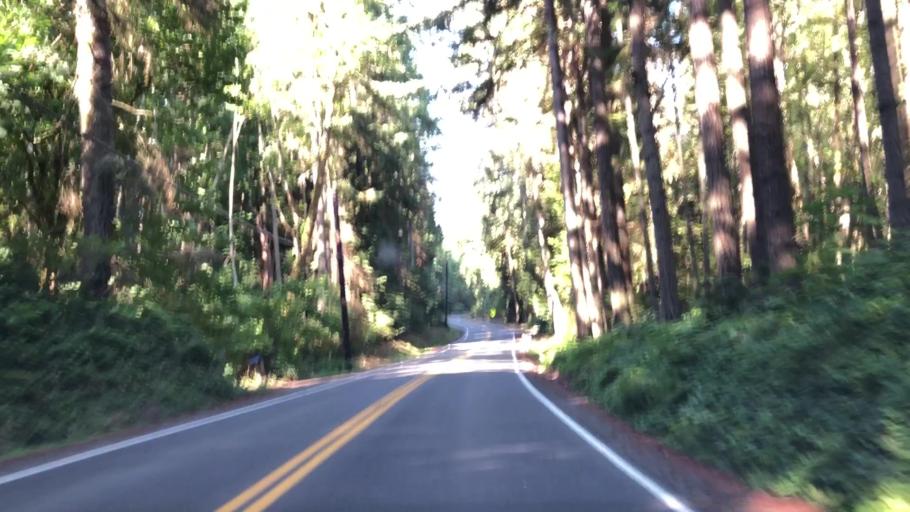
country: US
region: Washington
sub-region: Kitsap County
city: Indianola
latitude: 47.7666
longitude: -122.5174
